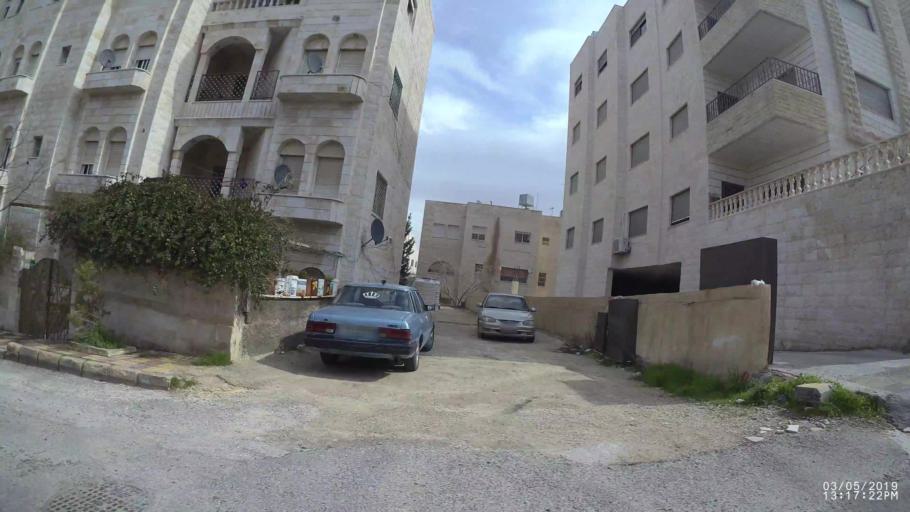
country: JO
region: Amman
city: Amman
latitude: 32.0002
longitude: 35.9345
